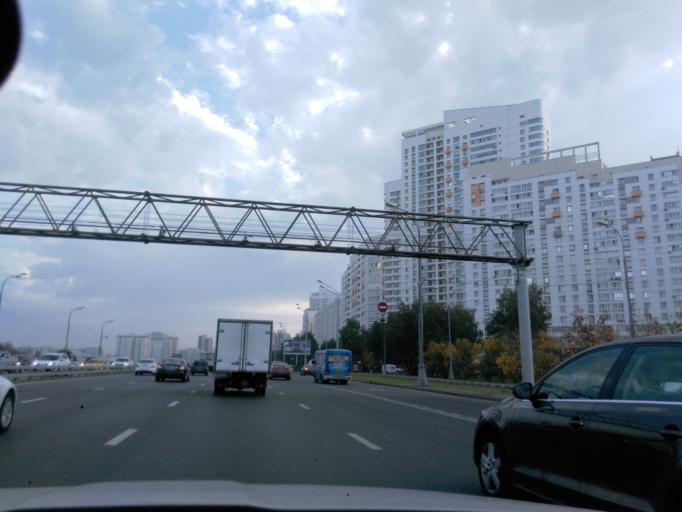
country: RU
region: Moscow
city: Troparevo
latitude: 55.6436
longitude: 37.4698
